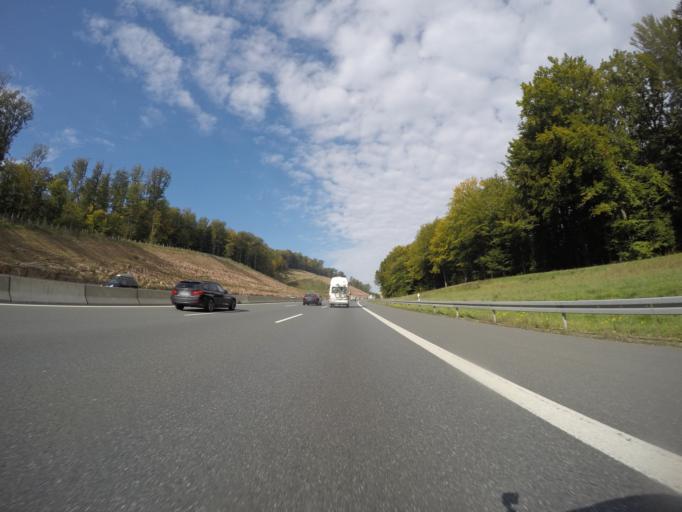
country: DE
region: Bavaria
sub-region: Regierungsbezirk Unterfranken
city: Altenbuch
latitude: 49.8848
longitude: 9.4205
